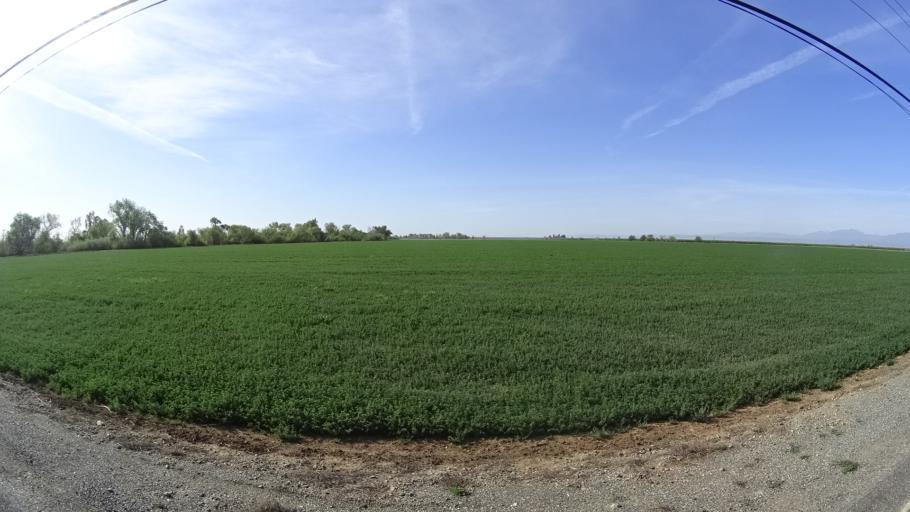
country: US
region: California
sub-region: Glenn County
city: Orland
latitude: 39.6684
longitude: -122.2198
